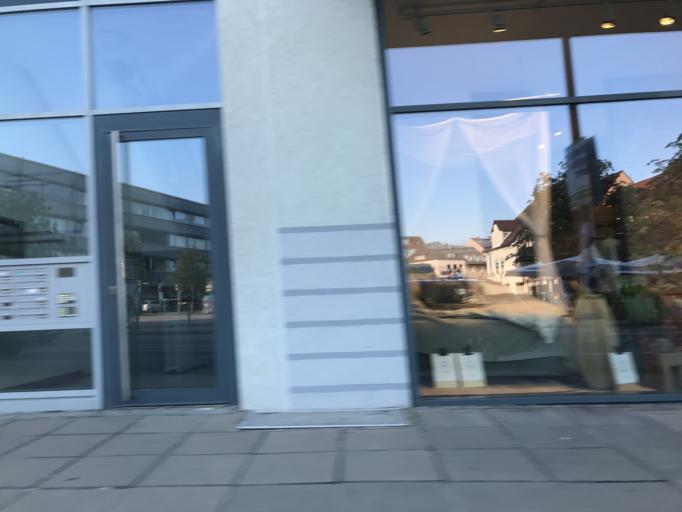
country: DE
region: Baden-Wuerttemberg
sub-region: Regierungsbezirk Stuttgart
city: Korntal
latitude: 48.8142
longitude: 9.1120
